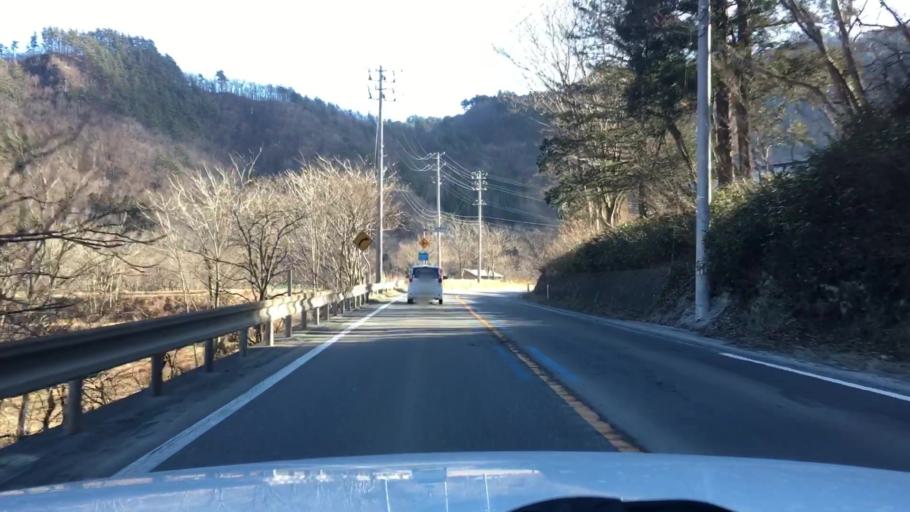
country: JP
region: Iwate
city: Miyako
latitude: 39.6051
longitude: 141.7725
